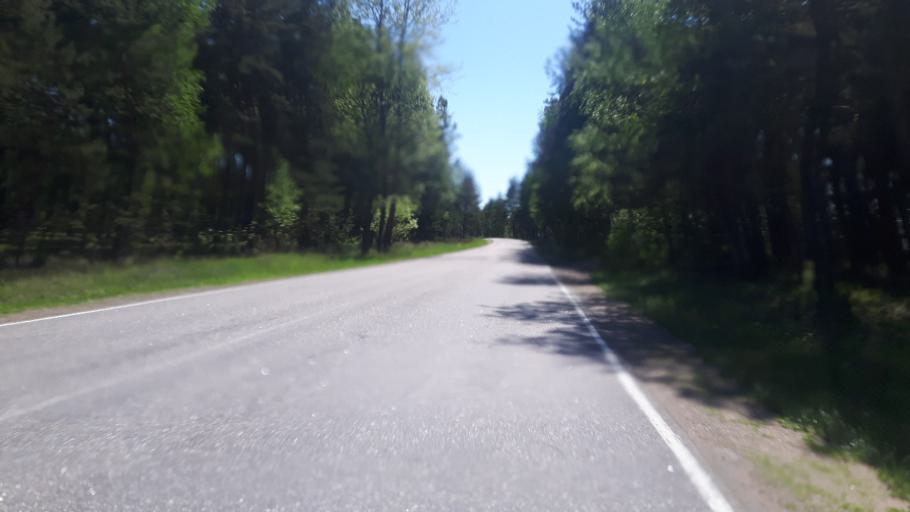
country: RU
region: Leningrad
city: Glebychevo
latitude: 60.3288
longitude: 28.8232
